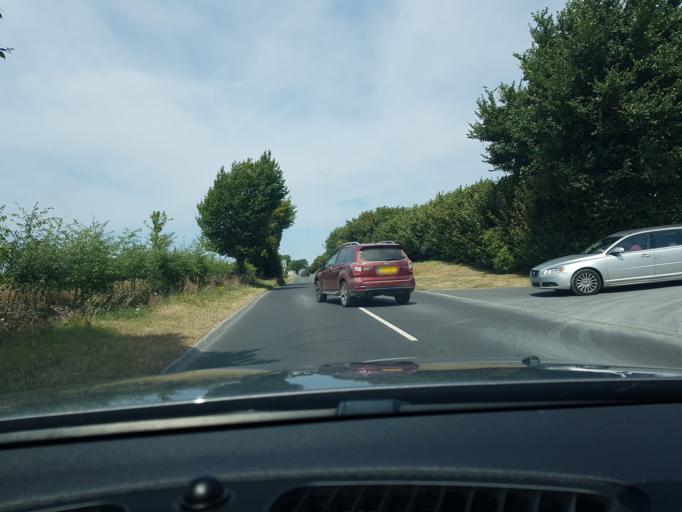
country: GB
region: England
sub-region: West Berkshire
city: Wickham
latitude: 51.4581
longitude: -1.4806
